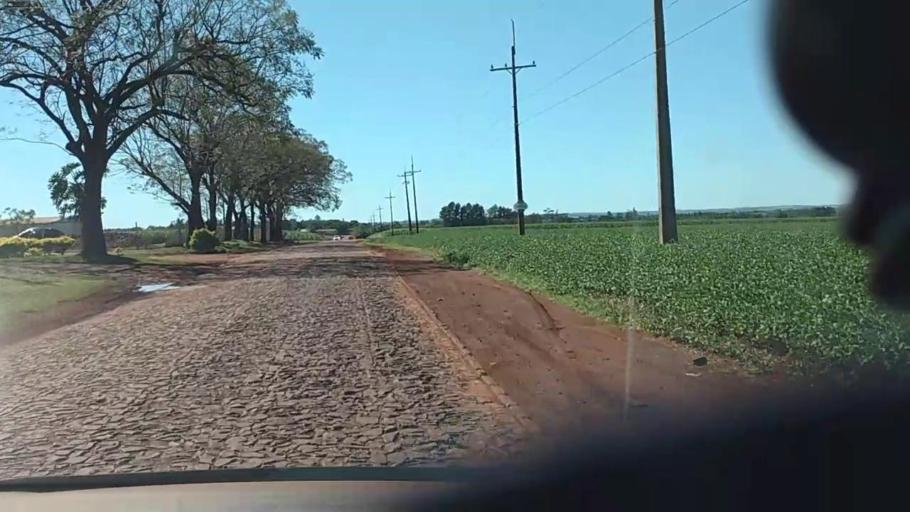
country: PY
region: Alto Parana
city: Naranjal
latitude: -25.9549
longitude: -55.1334
